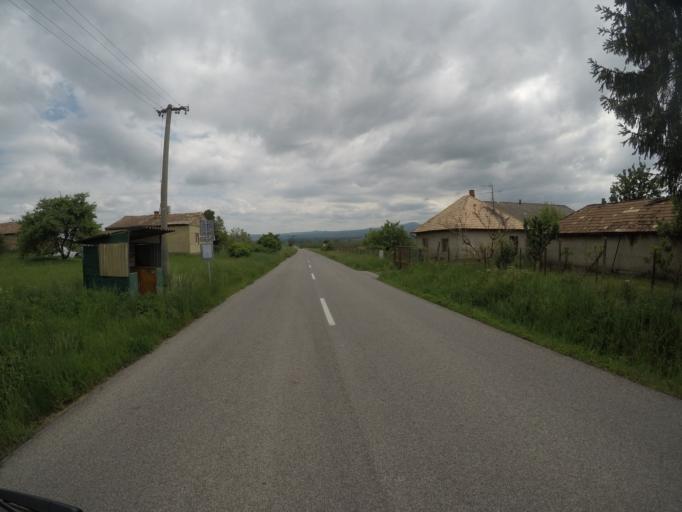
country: SK
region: Banskobystricky
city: Dudince
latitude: 48.0759
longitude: 18.8258
